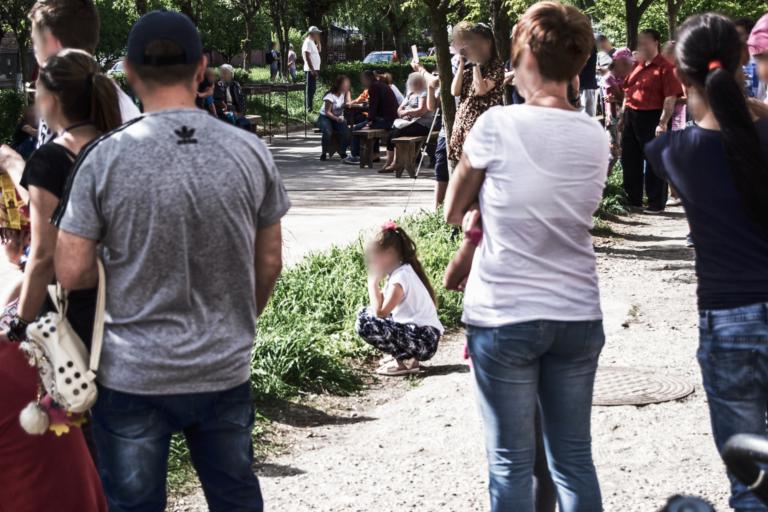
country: RO
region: Hunedoara
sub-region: Municipiul Petrosani
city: Petrosani
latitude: 45.4404
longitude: 23.3744
